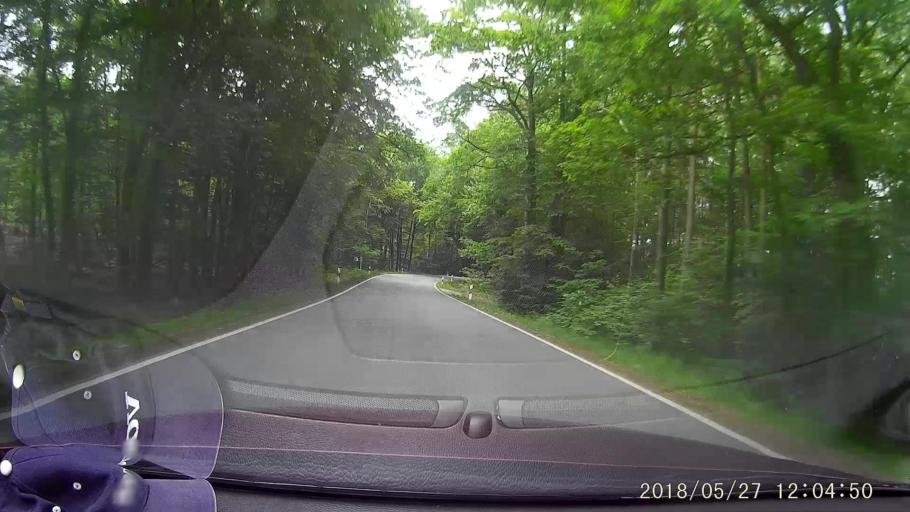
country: DE
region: Saxony
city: Mucka
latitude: 51.3460
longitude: 14.6729
